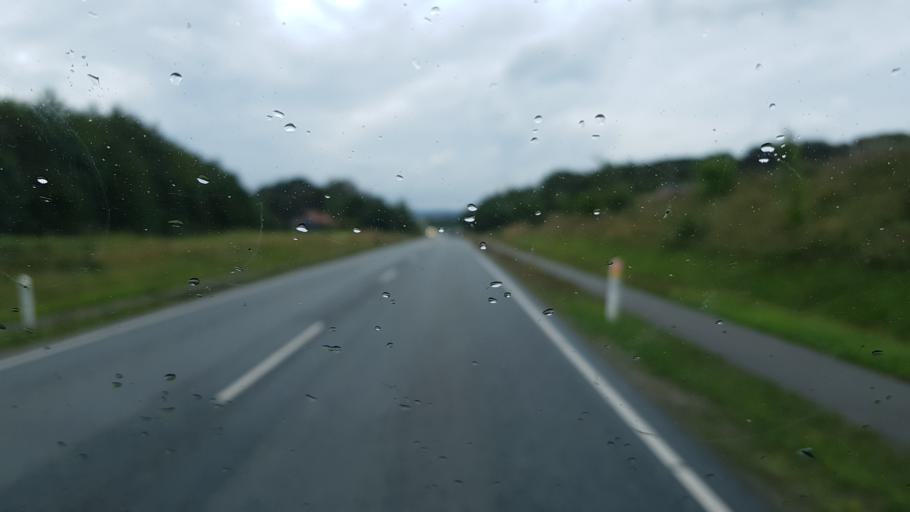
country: DK
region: Central Jutland
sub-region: Horsens Kommune
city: Horsens
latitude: 55.9015
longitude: 9.7466
